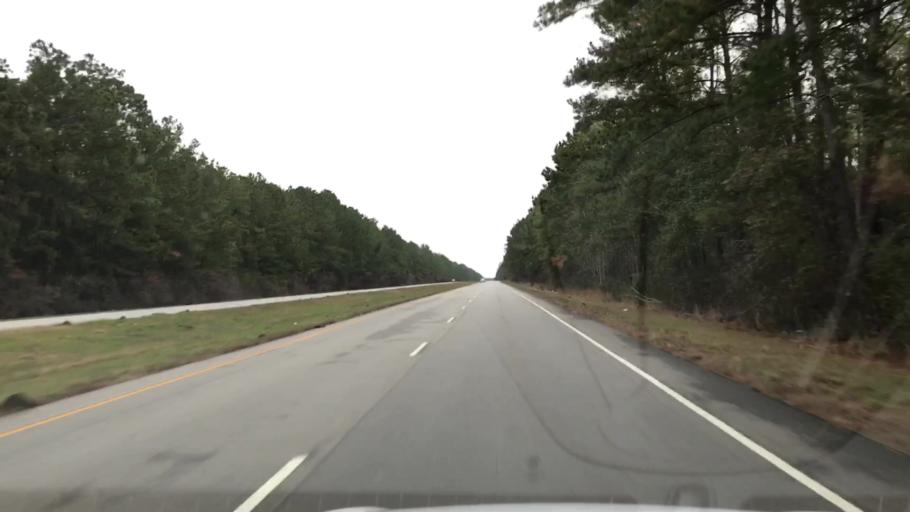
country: US
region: South Carolina
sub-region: Charleston County
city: Awendaw
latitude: 33.1488
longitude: -79.4342
